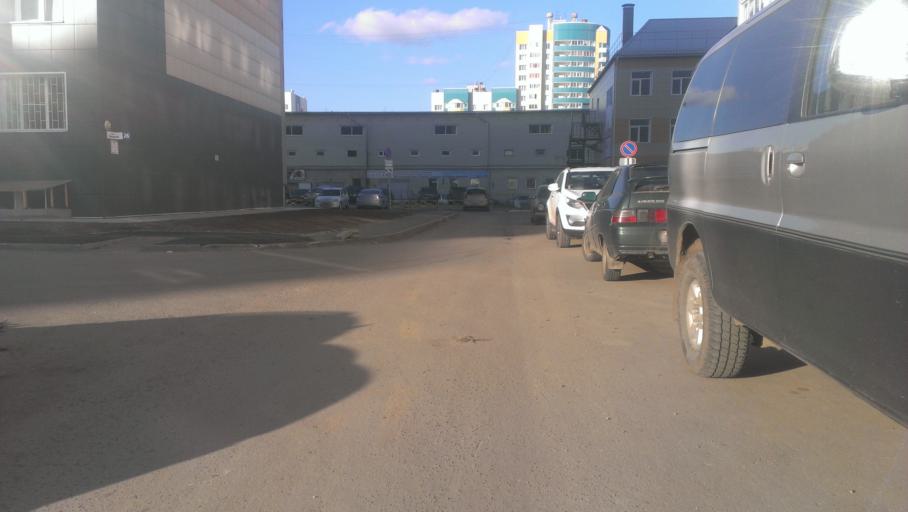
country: RU
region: Altai Krai
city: Novosilikatnyy
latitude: 53.3389
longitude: 83.6603
